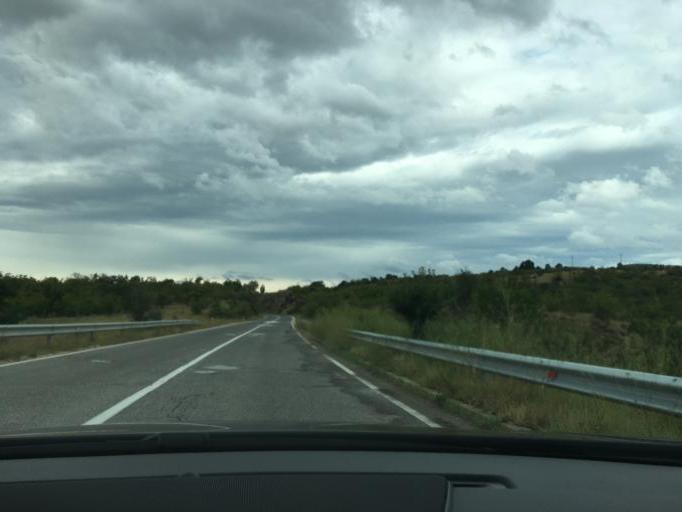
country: MK
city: Klechovce
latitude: 42.1532
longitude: 21.9522
